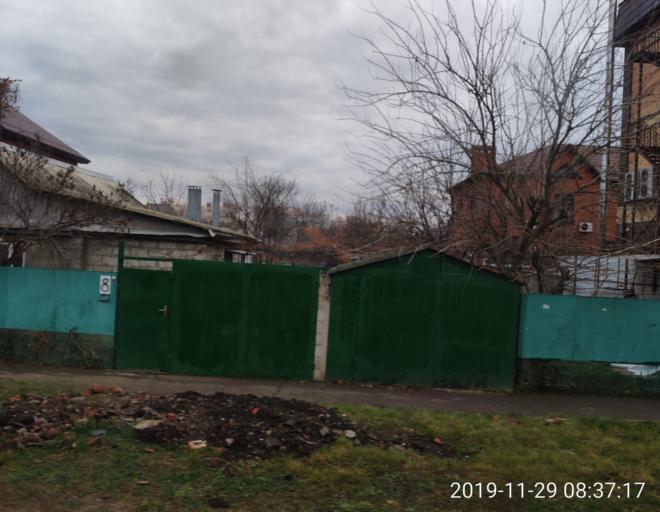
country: RU
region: Krasnodarskiy
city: Krasnodar
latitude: 45.0517
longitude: 39.0030
